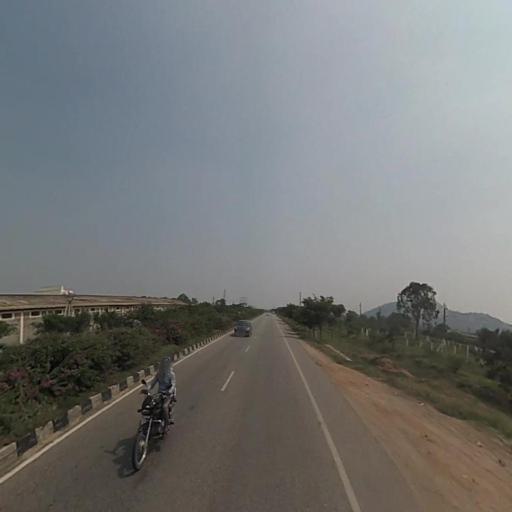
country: IN
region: Telangana
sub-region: Nalgonda
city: Nalgonda
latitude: 17.2125
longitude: 79.1636
